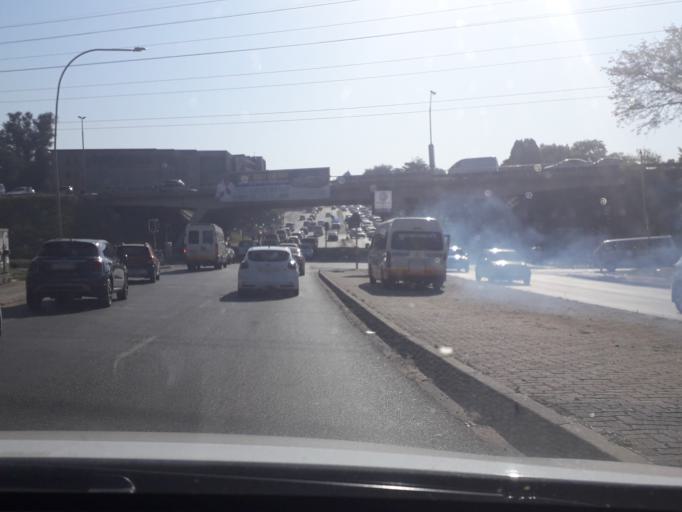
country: ZA
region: Gauteng
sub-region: City of Johannesburg Metropolitan Municipality
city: Johannesburg
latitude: -26.1288
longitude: 28.0710
